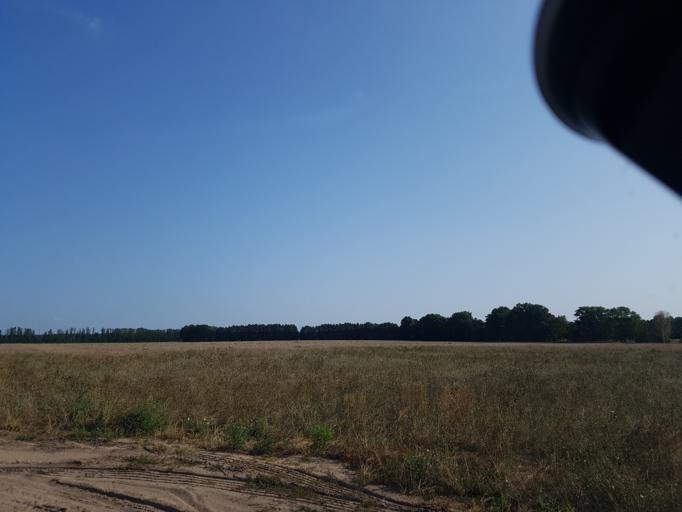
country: DE
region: Brandenburg
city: Wollin
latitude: 52.2847
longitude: 12.4681
